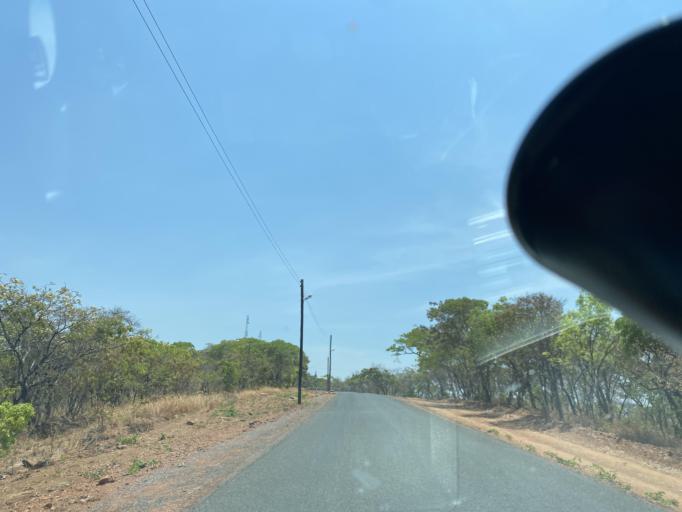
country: ZM
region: Lusaka
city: Kafue
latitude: -15.8650
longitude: 28.4549
